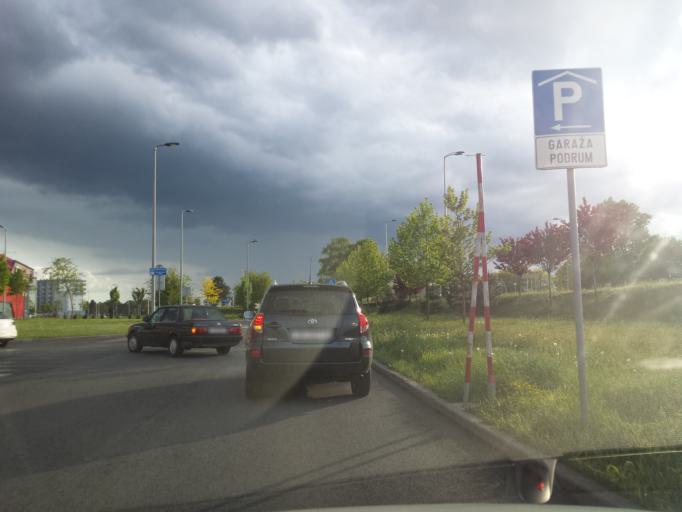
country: HR
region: Grad Zagreb
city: Jankomir
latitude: 45.7718
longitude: 15.9391
